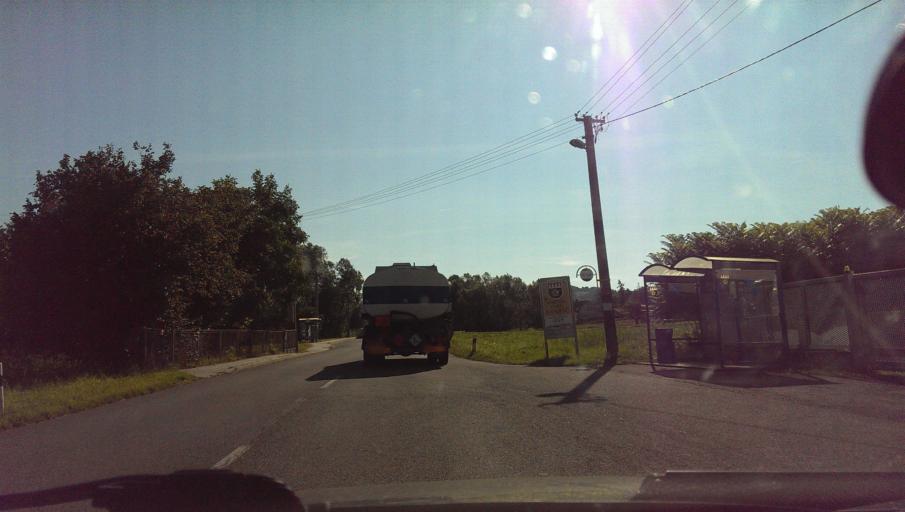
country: CZ
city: Frycovice
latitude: 49.6838
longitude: 18.2432
